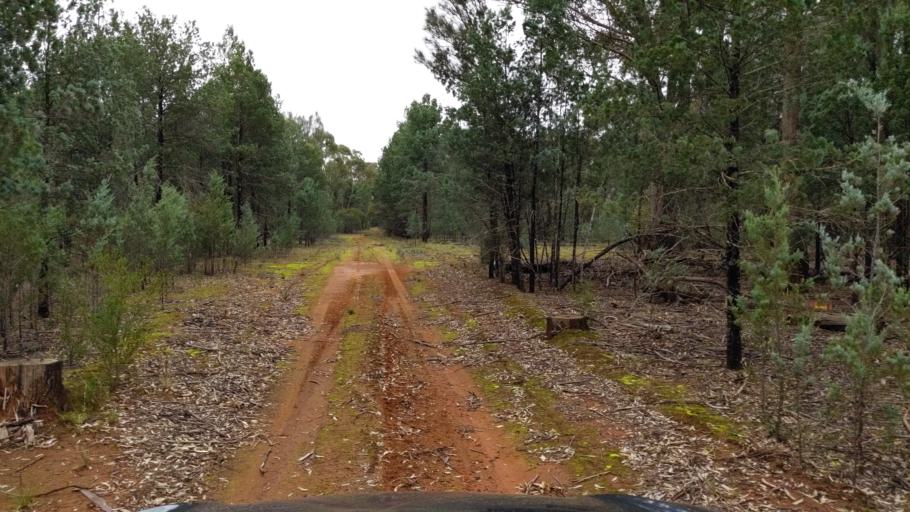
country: AU
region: New South Wales
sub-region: Coolamon
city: Coolamon
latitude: -34.8442
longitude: 146.9331
